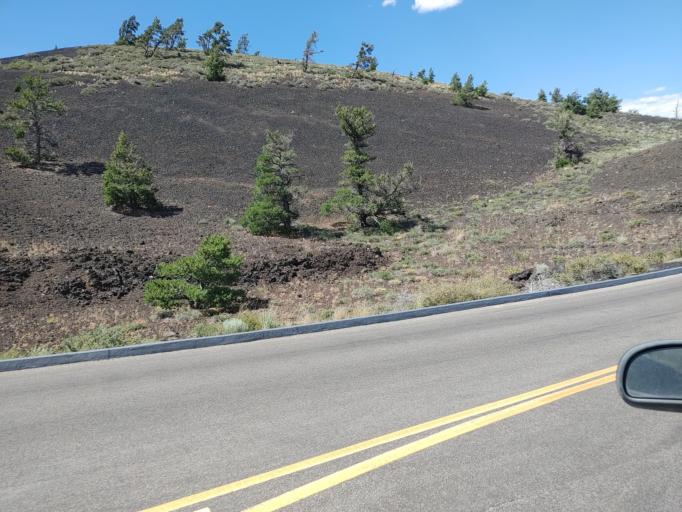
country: US
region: Idaho
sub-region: Butte County
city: Arco
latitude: 43.4424
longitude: -113.5572
